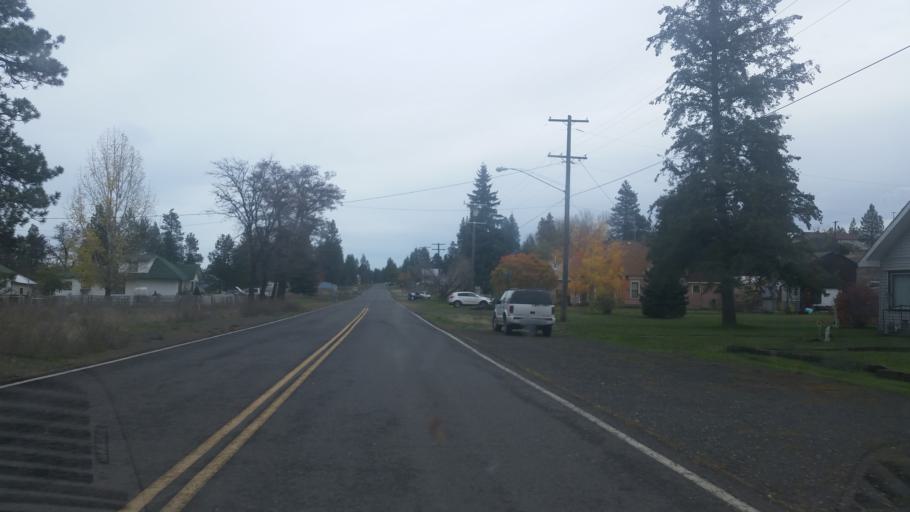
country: US
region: Washington
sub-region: Spokane County
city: Cheney
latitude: 47.2286
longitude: -117.4811
